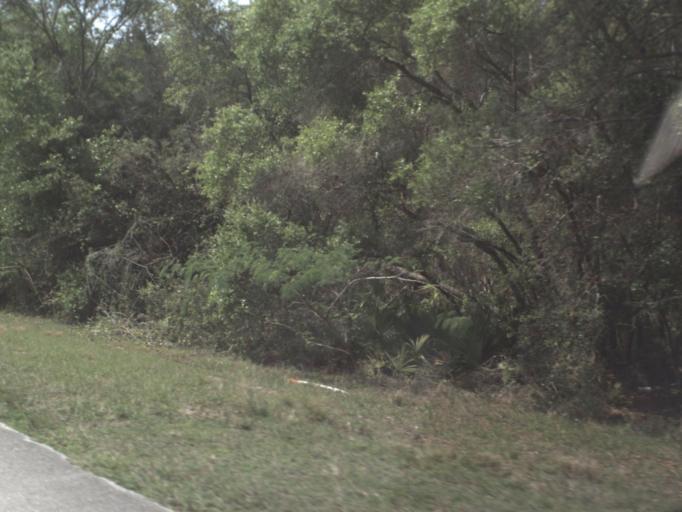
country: US
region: Florida
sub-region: Lake County
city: Astor
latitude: 29.2672
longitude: -81.6466
